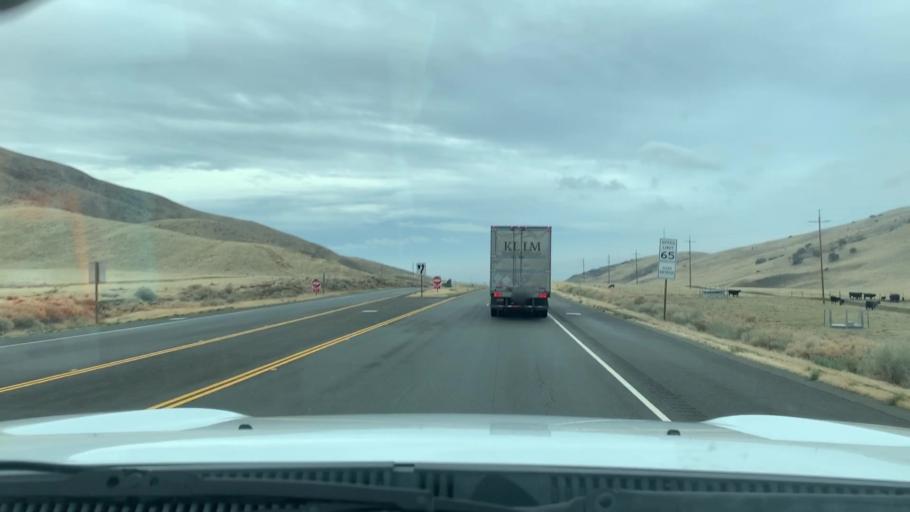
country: US
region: California
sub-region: San Luis Obispo County
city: Shandon
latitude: 35.7254
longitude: -120.1916
